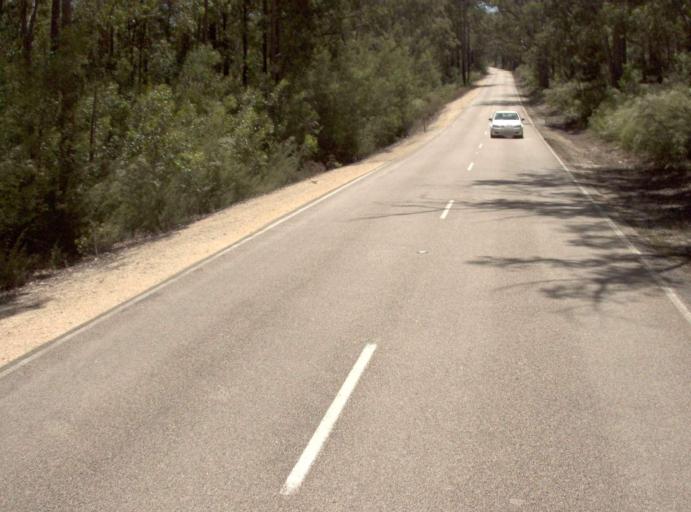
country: AU
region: Victoria
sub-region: East Gippsland
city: Lakes Entrance
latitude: -37.6450
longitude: 147.8945
